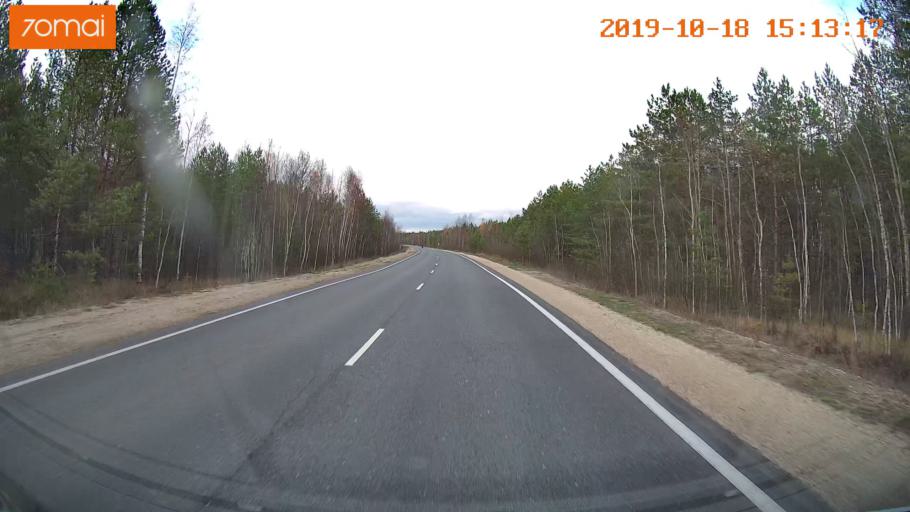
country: RU
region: Vladimir
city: Gus'-Khrustal'nyy
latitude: 55.5846
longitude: 40.7149
